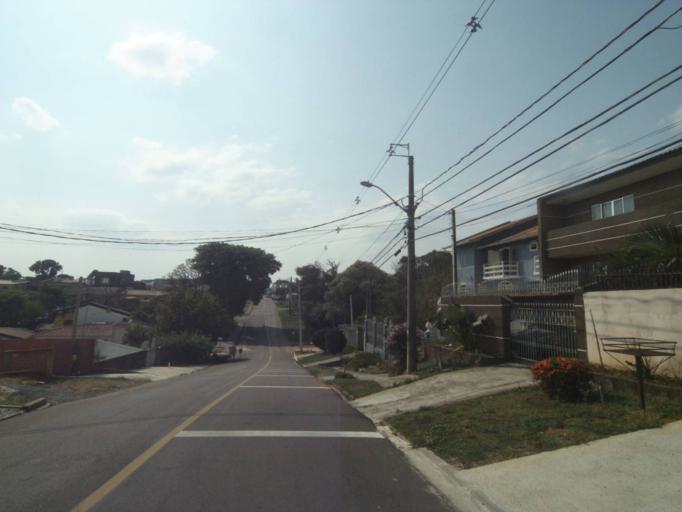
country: BR
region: Parana
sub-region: Sao Jose Dos Pinhais
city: Sao Jose dos Pinhais
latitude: -25.5182
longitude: -49.2467
